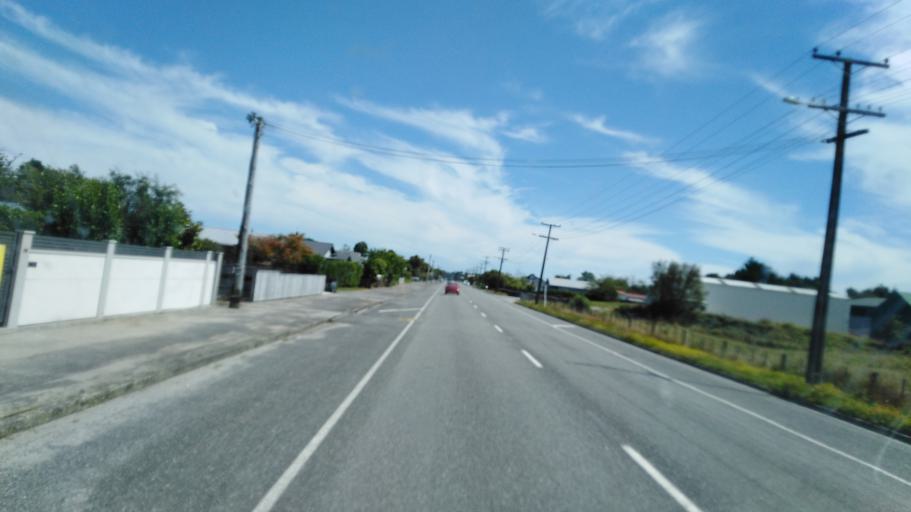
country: NZ
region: West Coast
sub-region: Buller District
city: Westport
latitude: -41.7532
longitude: 171.6162
